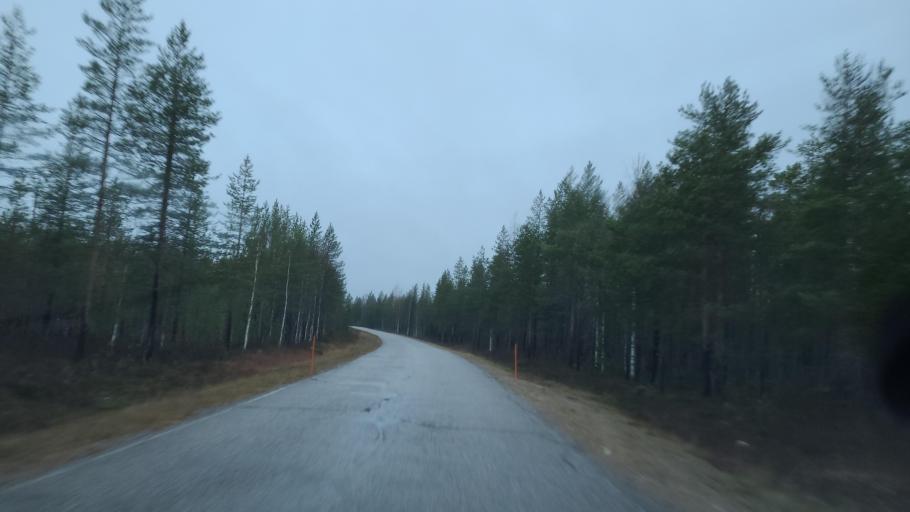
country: FI
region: Lapland
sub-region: Kemi-Tornio
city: Simo
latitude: 65.8854
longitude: 25.2209
